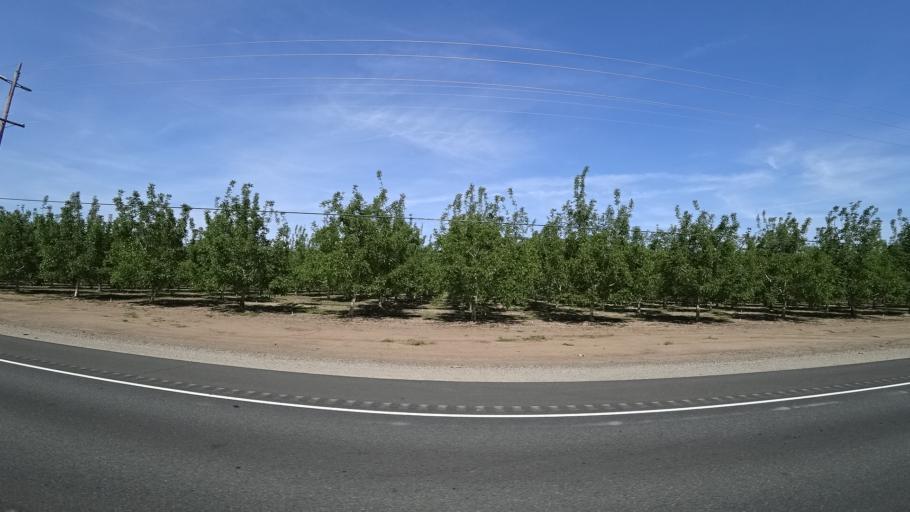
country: US
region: California
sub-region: Glenn County
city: Hamilton City
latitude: 39.8731
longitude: -121.9680
